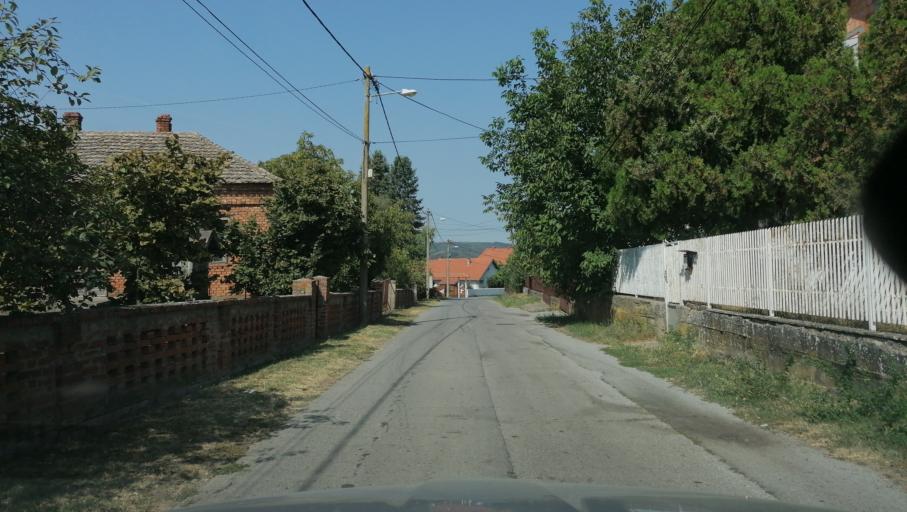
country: RS
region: Central Serbia
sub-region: Belgrade
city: Zvezdara
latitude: 44.6980
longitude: 20.5506
